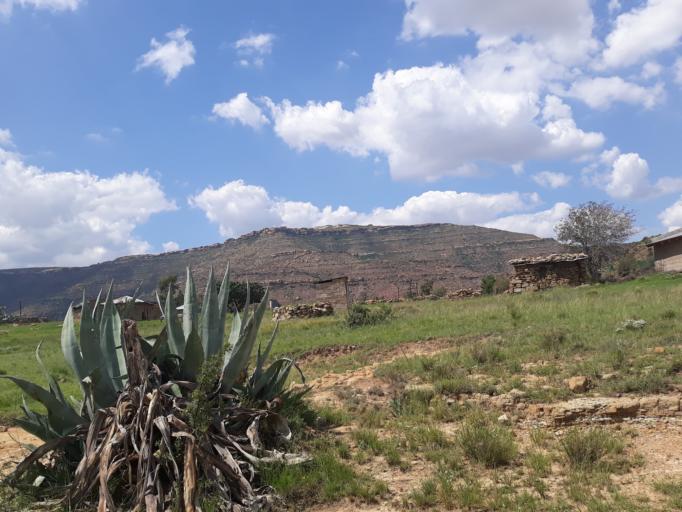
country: LS
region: Quthing
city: Quthing
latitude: -30.3425
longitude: 27.5280
